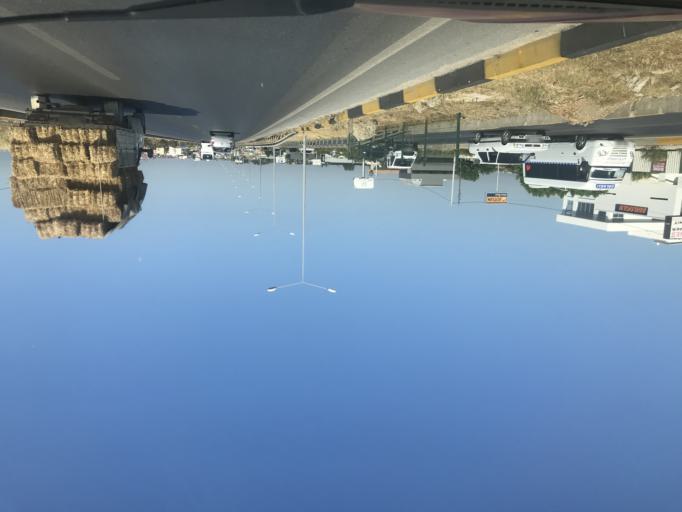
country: TR
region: Antalya
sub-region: Manavgat
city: Side
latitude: 36.8042
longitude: 31.3934
